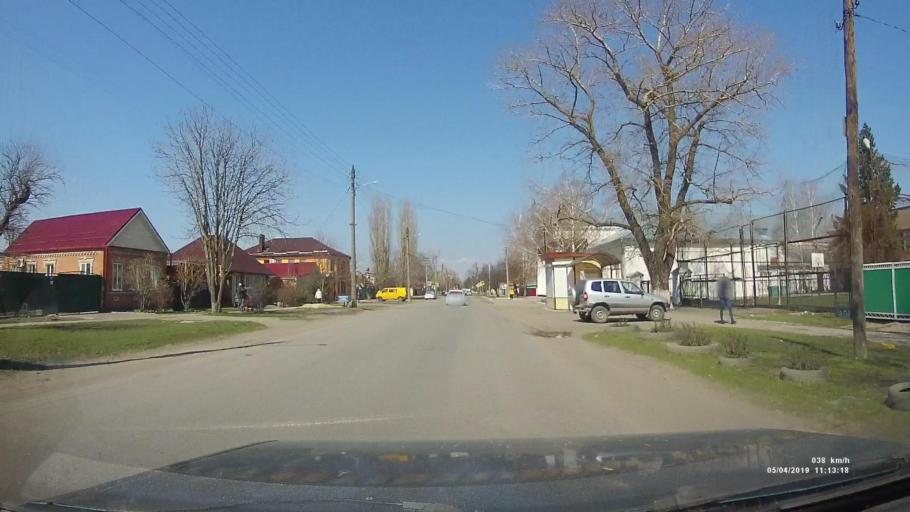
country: RU
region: Rostov
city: Azov
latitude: 47.1017
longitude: 39.4321
